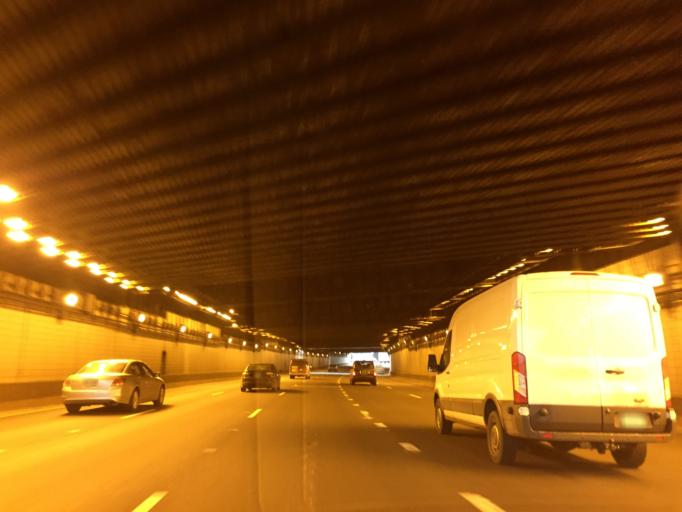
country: US
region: Illinois
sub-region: Cook County
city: Chicago
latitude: 41.8890
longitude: -87.6483
